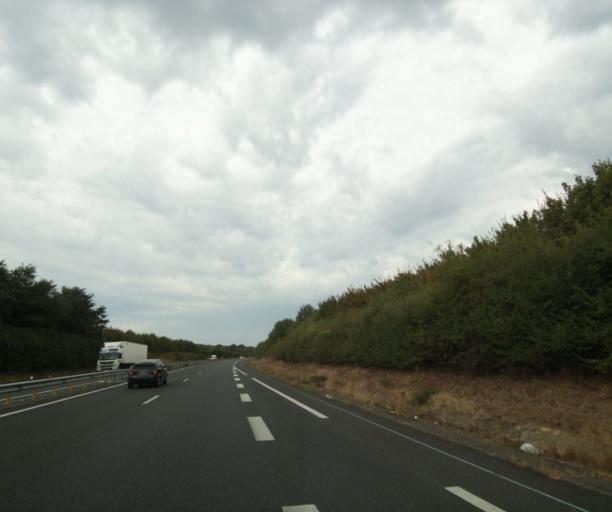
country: FR
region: Poitou-Charentes
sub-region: Departement de la Charente-Maritime
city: Tonnay-Charente
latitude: 45.9550
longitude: -0.8918
